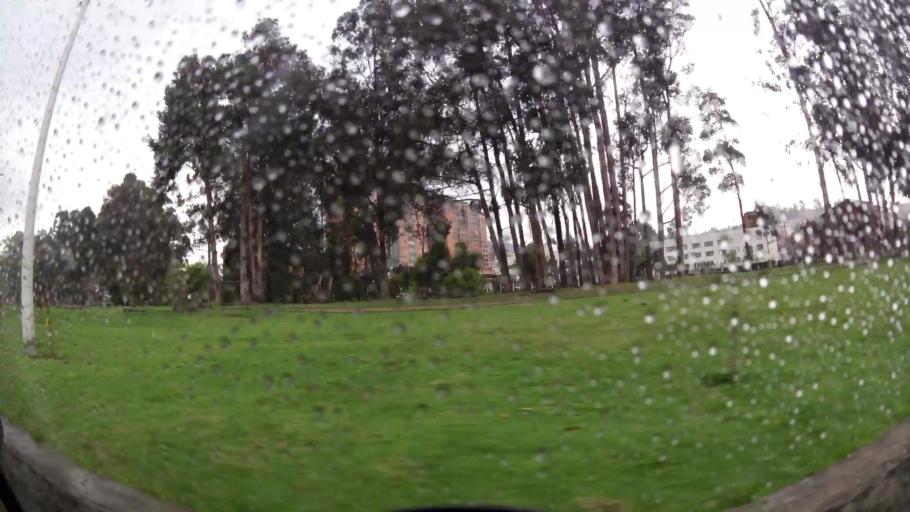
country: EC
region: Azuay
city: Cuenca
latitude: -2.8911
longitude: -79.0316
